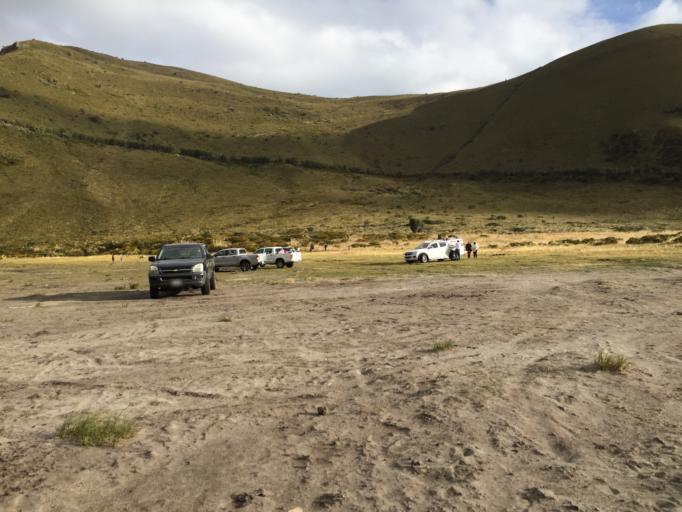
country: EC
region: Imbabura
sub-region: Canton Otavalo
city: Otavalo
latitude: 0.1135
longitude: -78.2747
